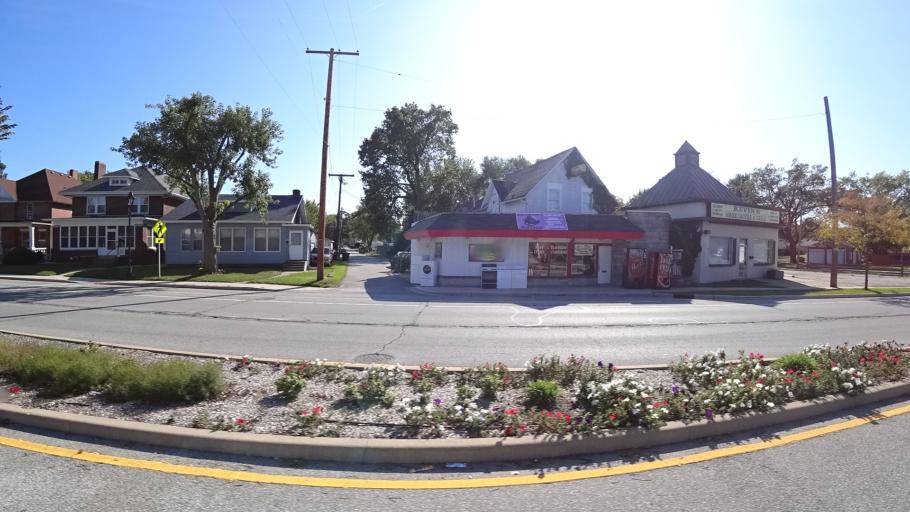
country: US
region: Indiana
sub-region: LaPorte County
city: Michigan City
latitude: 41.7105
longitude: -86.8766
